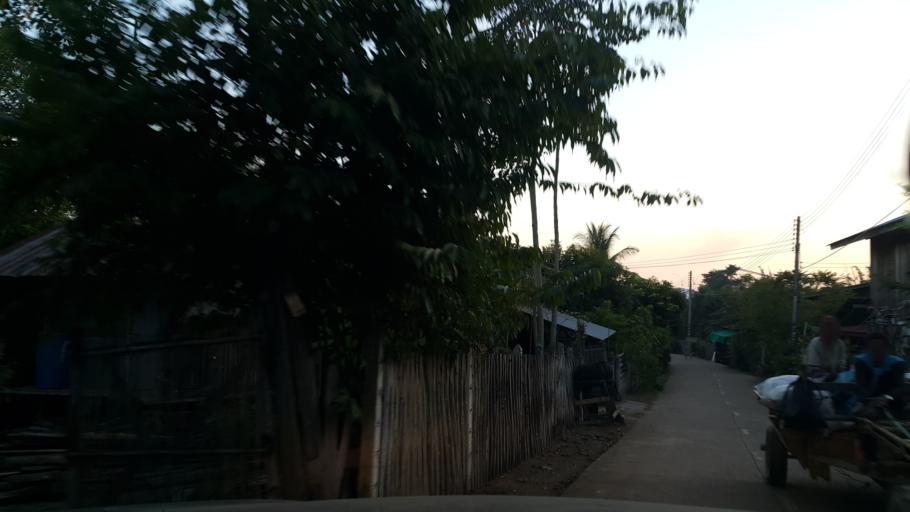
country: TH
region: Phrae
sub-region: Amphoe Wang Chin
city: Wang Chin
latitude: 17.8757
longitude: 99.6223
